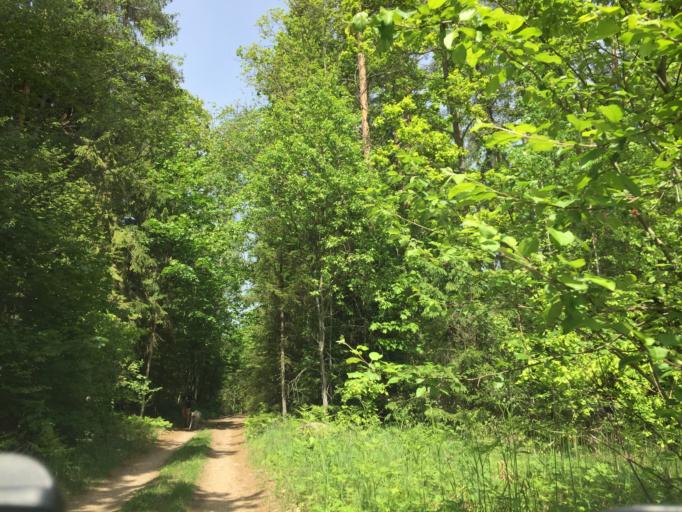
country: LV
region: Koceni
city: Koceni
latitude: 57.4397
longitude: 25.2842
